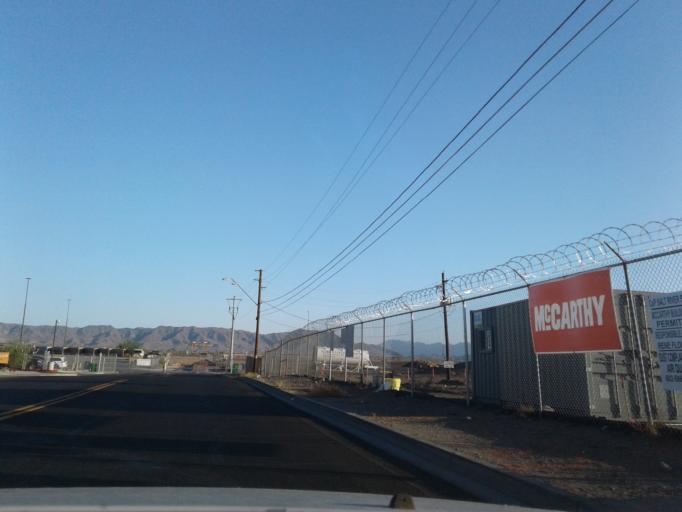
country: US
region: Arizona
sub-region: Maricopa County
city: Phoenix
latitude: 33.4206
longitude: -112.1071
